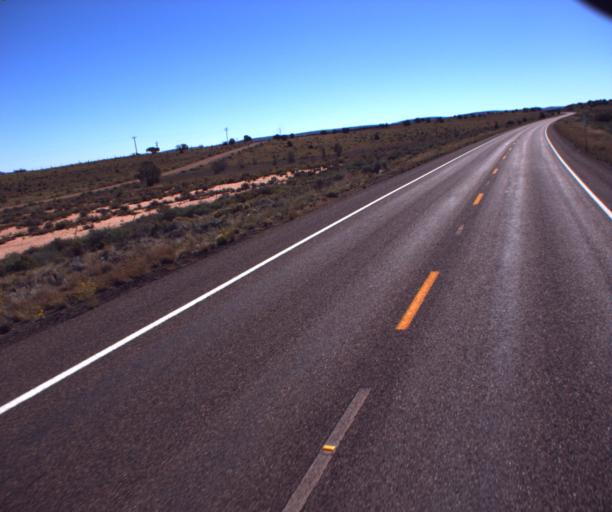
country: US
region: Arizona
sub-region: Apache County
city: Saint Johns
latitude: 34.6122
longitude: -109.6515
